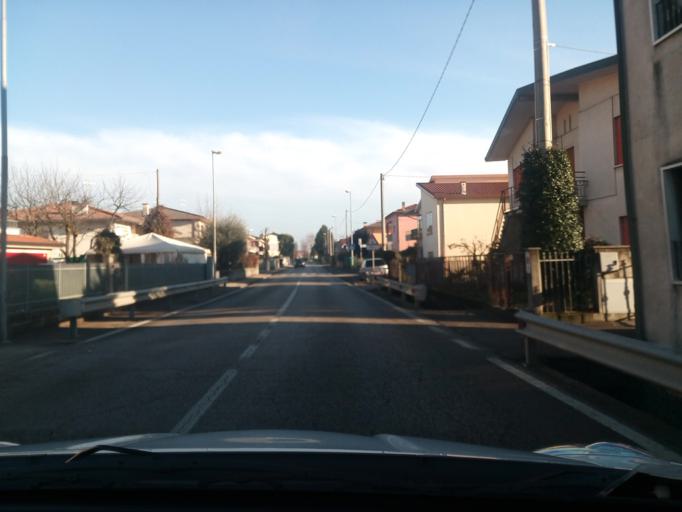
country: IT
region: Veneto
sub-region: Provincia di Vicenza
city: Dueville
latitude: 45.6406
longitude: 11.5428
